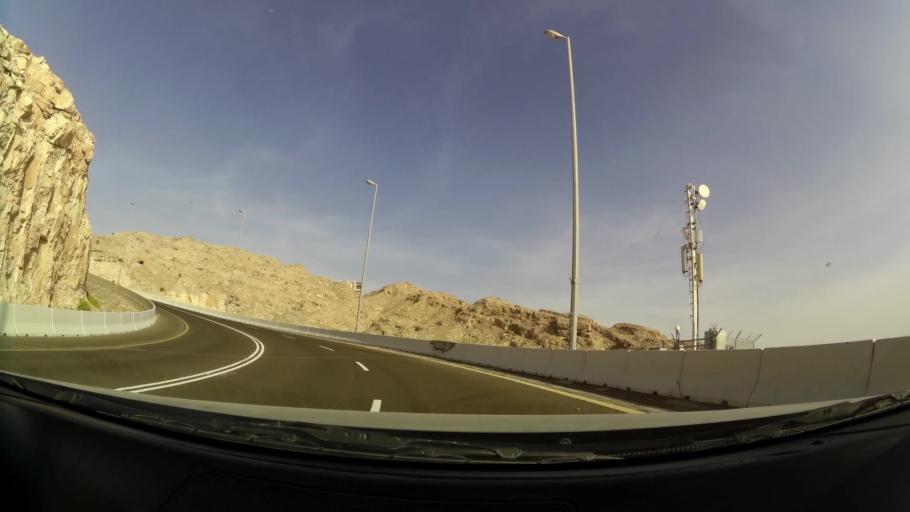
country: AE
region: Abu Dhabi
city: Al Ain
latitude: 24.0832
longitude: 55.7623
